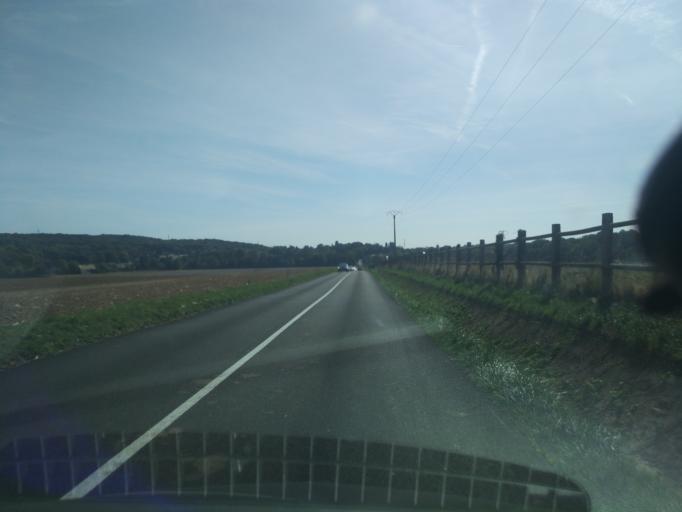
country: FR
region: Ile-de-France
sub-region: Departement de l'Essonne
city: Forges-les-Bains
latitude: 48.6341
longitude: 2.1096
